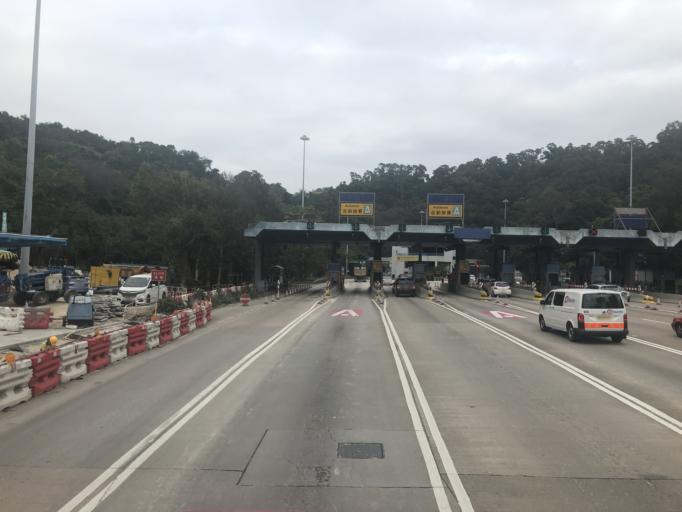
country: HK
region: Kowloon City
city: Kowloon
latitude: 22.3158
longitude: 114.2404
